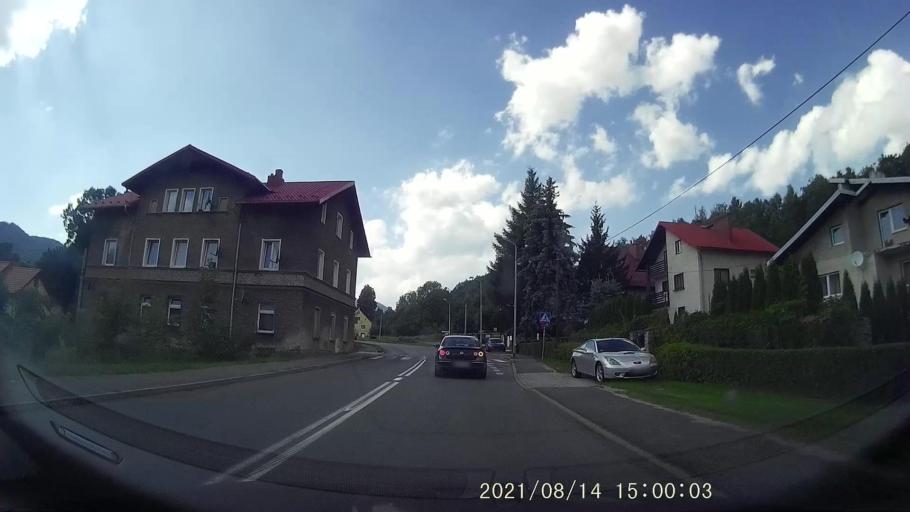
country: PL
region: Lower Silesian Voivodeship
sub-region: Powiat walbrzyski
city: Jedlina-Zdroj
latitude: 50.7140
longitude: 16.3617
